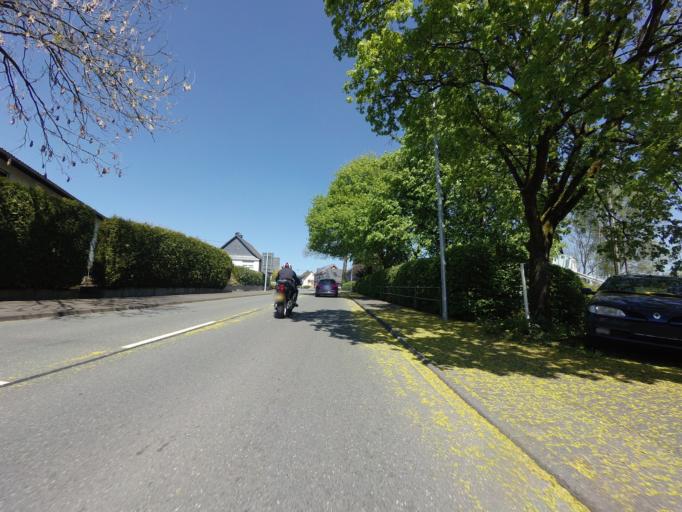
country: DE
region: North Rhine-Westphalia
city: Kreuztal
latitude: 50.9952
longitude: 7.9573
